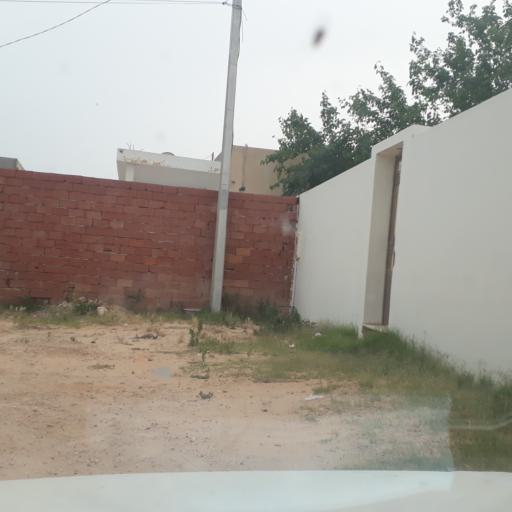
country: TN
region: Safaqis
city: Al Qarmadah
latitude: 34.8240
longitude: 10.7789
